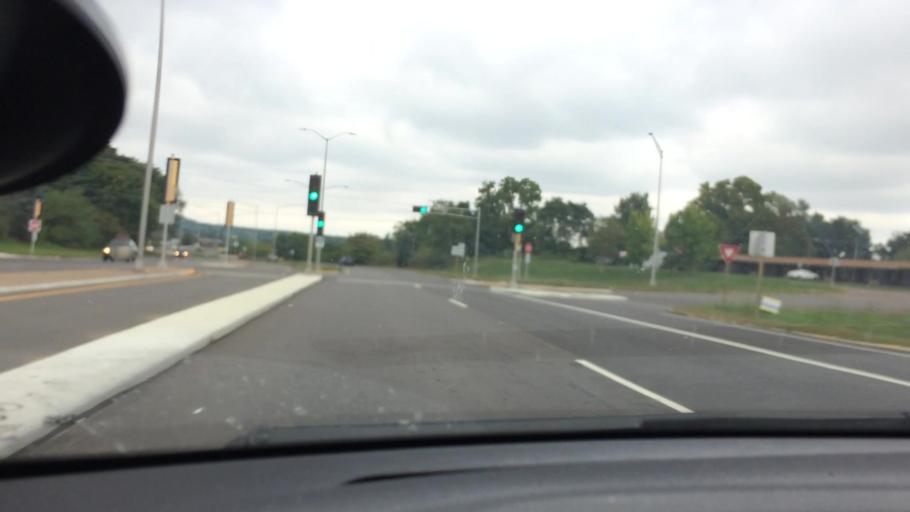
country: US
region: Wisconsin
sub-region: Chippewa County
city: Chippewa Falls
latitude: 44.9255
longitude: -91.3828
